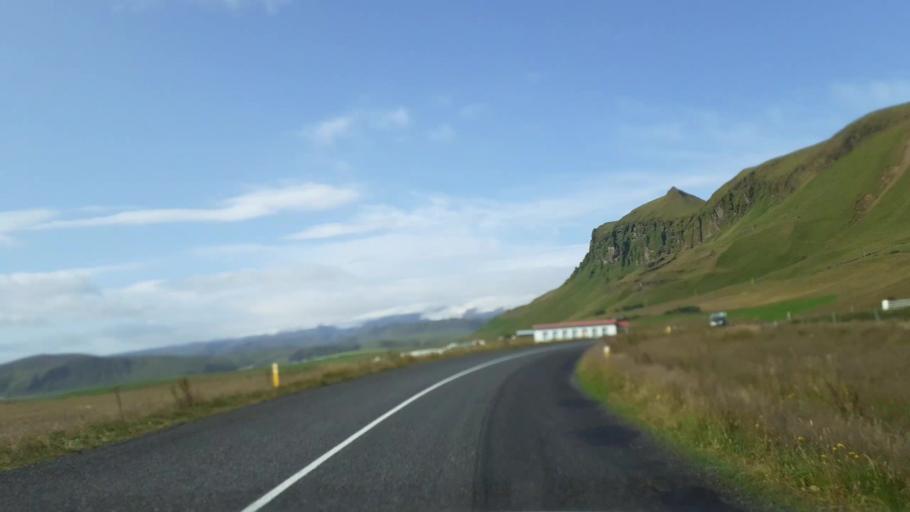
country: IS
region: South
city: Vestmannaeyjar
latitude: 63.4179
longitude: -19.0487
